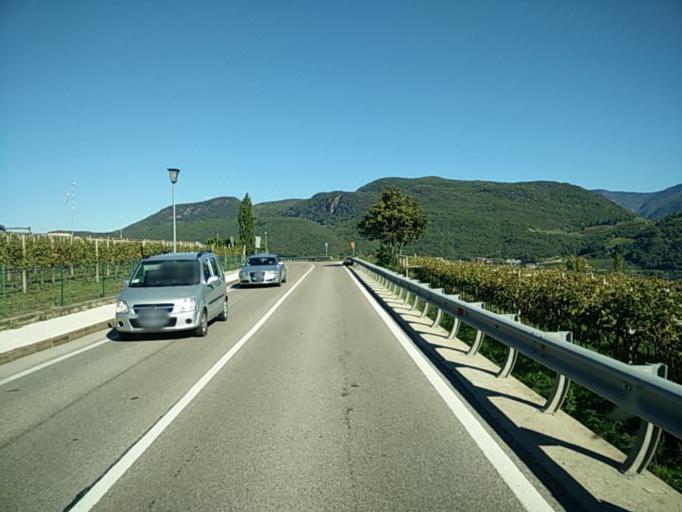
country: IT
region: Trentino-Alto Adige
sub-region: Bolzano
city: Caldaro sulla Strada del Vino
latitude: 46.3785
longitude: 11.2530
